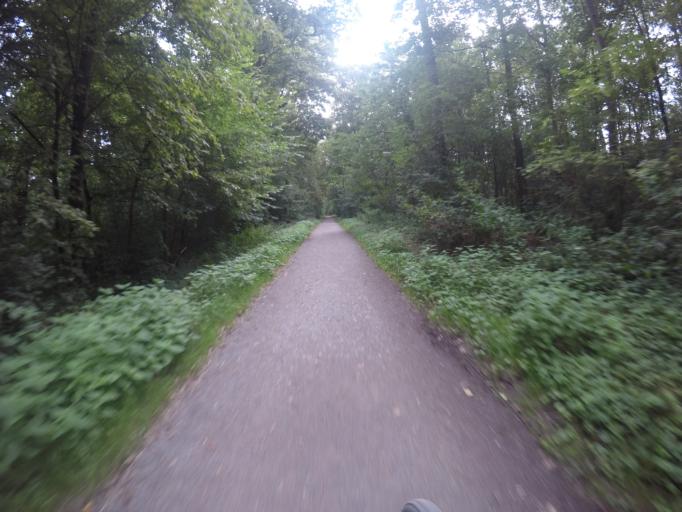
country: DE
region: Baden-Wuerttemberg
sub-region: Regierungsbezirk Stuttgart
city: Leinfelden-Echterdingen
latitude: 48.7395
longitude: 9.1414
